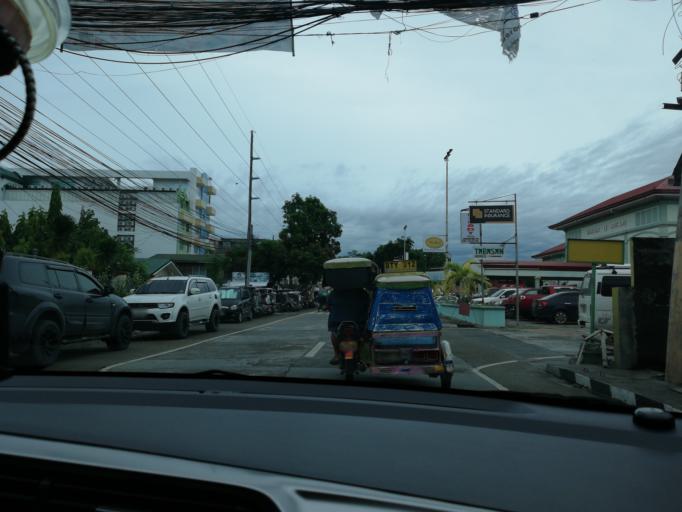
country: PH
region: Ilocos
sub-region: Province of Ilocos Sur
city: Vigan
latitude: 17.5798
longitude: 120.3867
